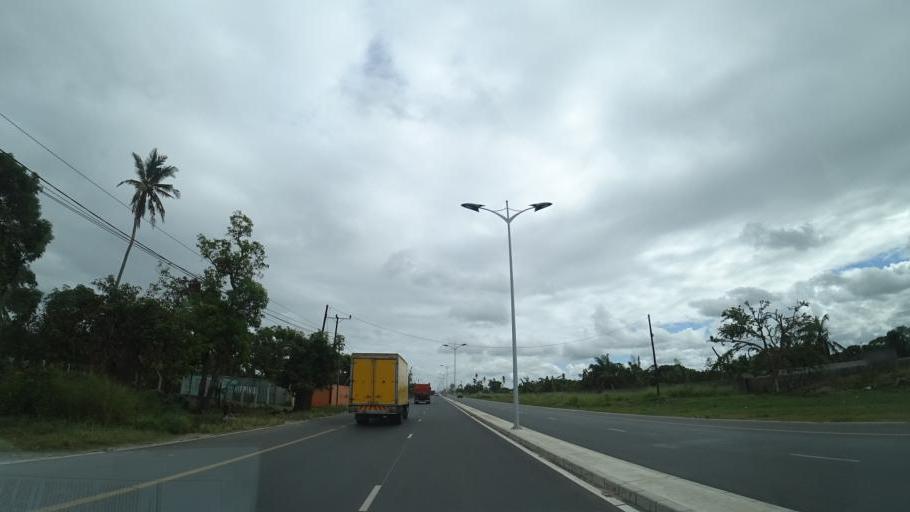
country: MZ
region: Sofala
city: Dondo
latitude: -19.7146
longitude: 34.8002
